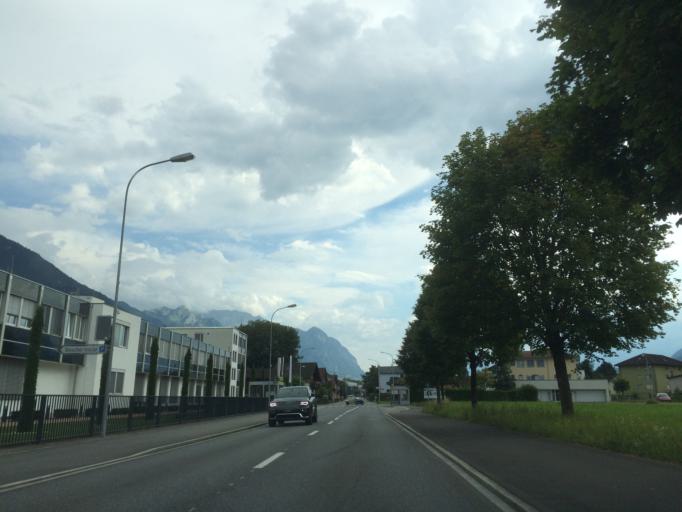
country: LI
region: Schaan
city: Schaan
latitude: 47.1728
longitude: 9.5089
